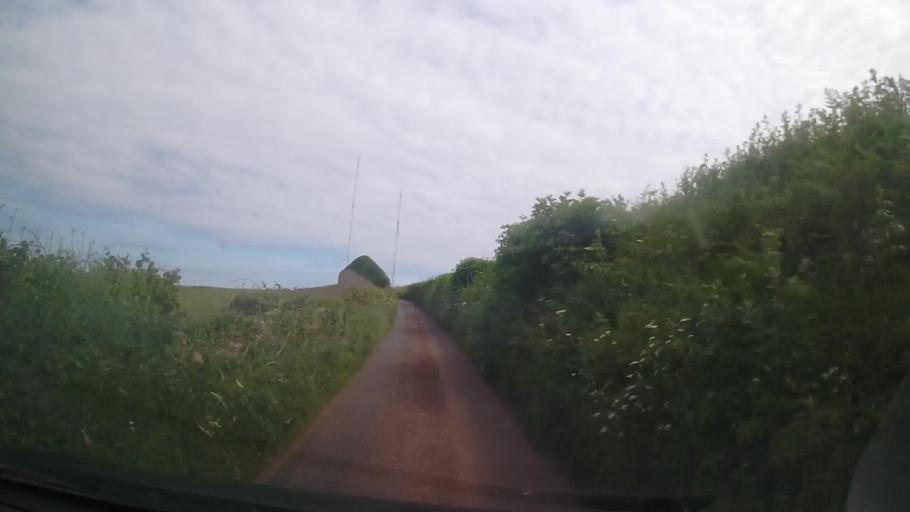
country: GB
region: England
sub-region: Devon
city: Salcombe
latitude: 50.2317
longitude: -3.6694
